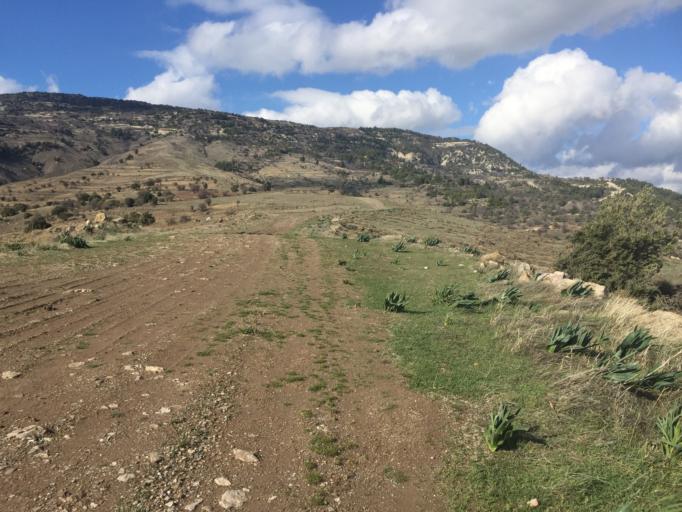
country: CY
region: Limassol
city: Pachna
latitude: 34.8830
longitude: 32.6549
